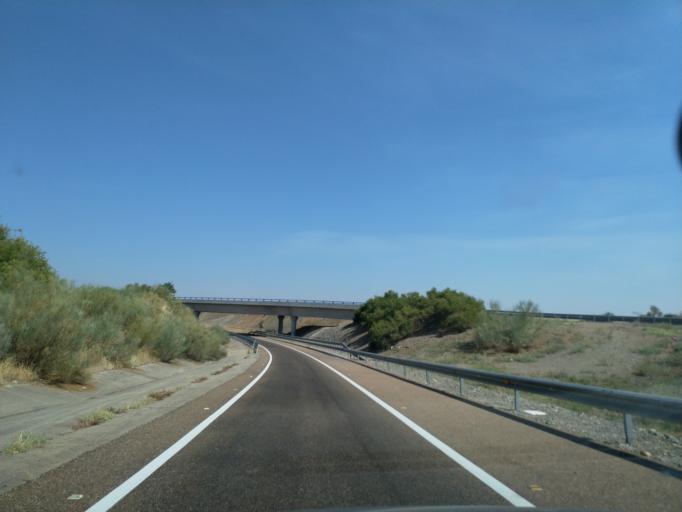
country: ES
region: Extremadura
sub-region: Provincia de Badajoz
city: Merida
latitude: 38.9460
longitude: -6.3414
